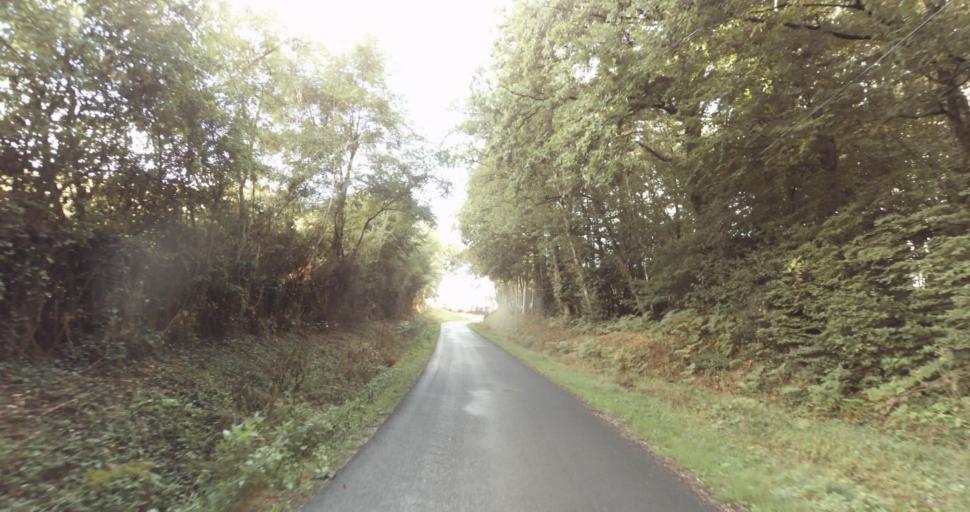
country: FR
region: Lower Normandy
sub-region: Departement de l'Orne
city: Gace
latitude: 48.8796
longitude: 0.3172
